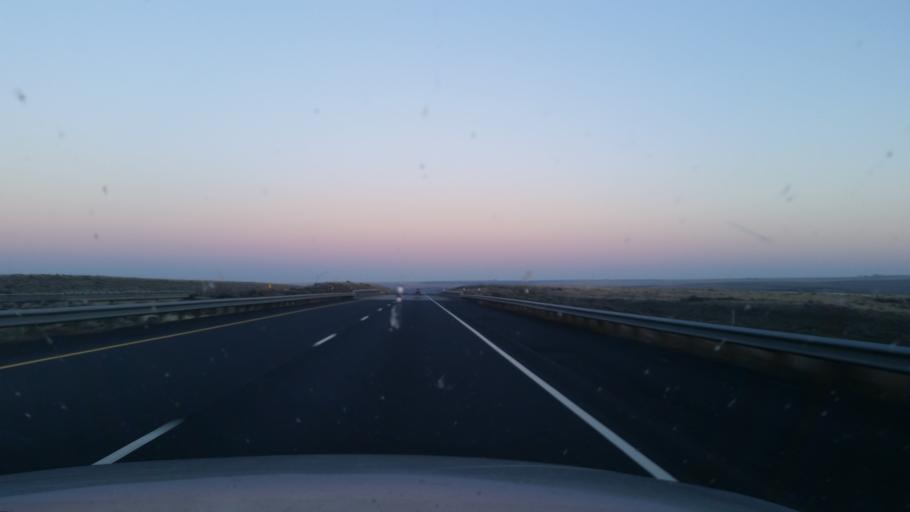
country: US
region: Washington
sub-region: Adams County
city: Ritzville
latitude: 47.0969
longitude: -118.6693
